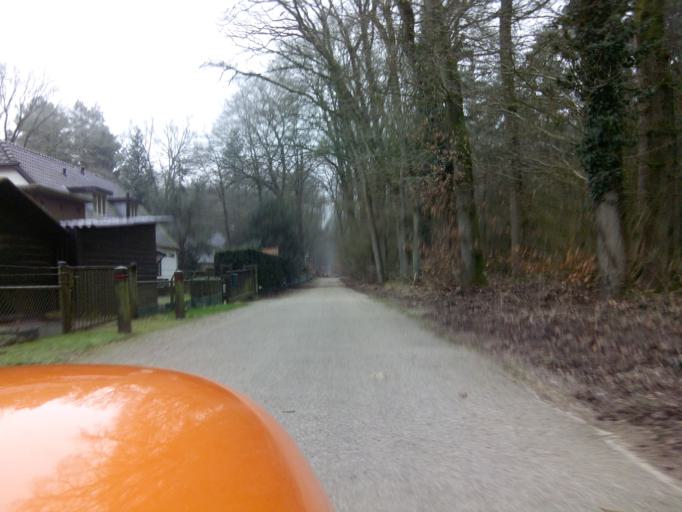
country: NL
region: Gelderland
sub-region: Gemeente Barneveld
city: Stroe
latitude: 52.2183
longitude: 5.6558
